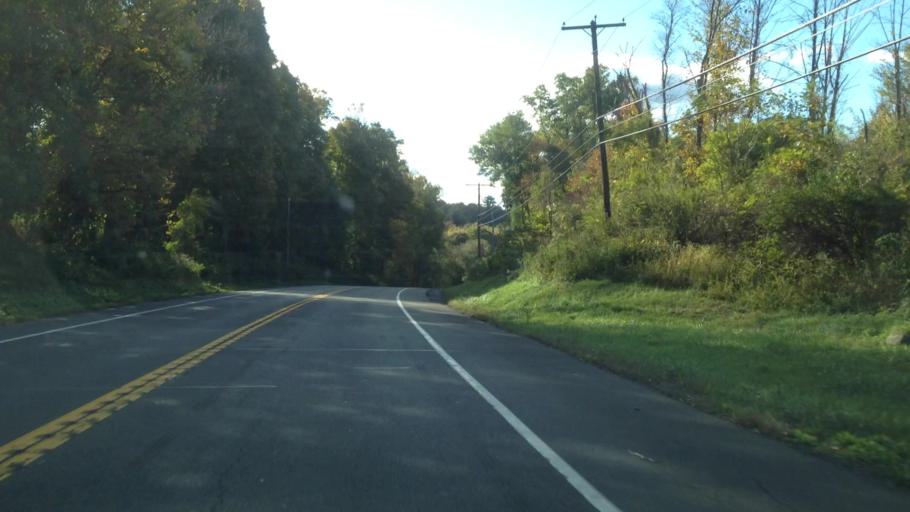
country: US
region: New York
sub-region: Dutchess County
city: Hyde Park
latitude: 41.8236
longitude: -73.9655
